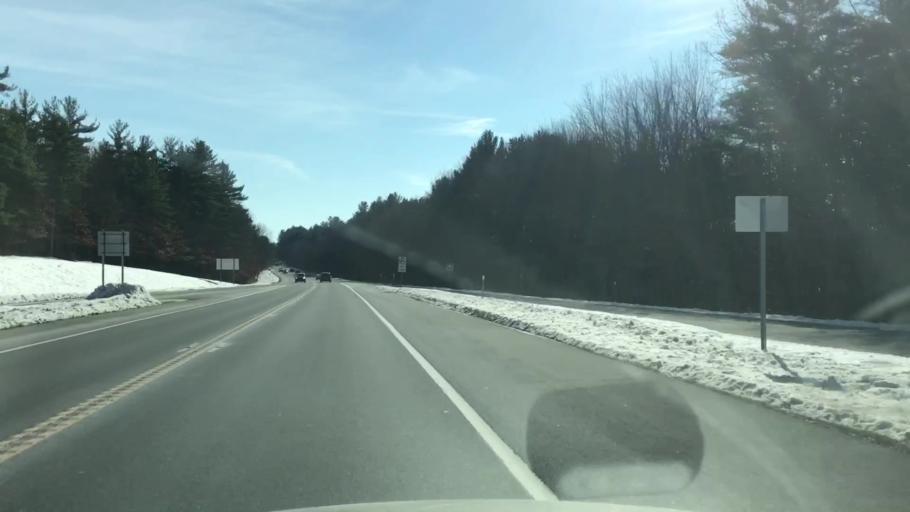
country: US
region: New Hampshire
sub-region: Hillsborough County
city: Milford
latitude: 42.8634
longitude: -71.6132
